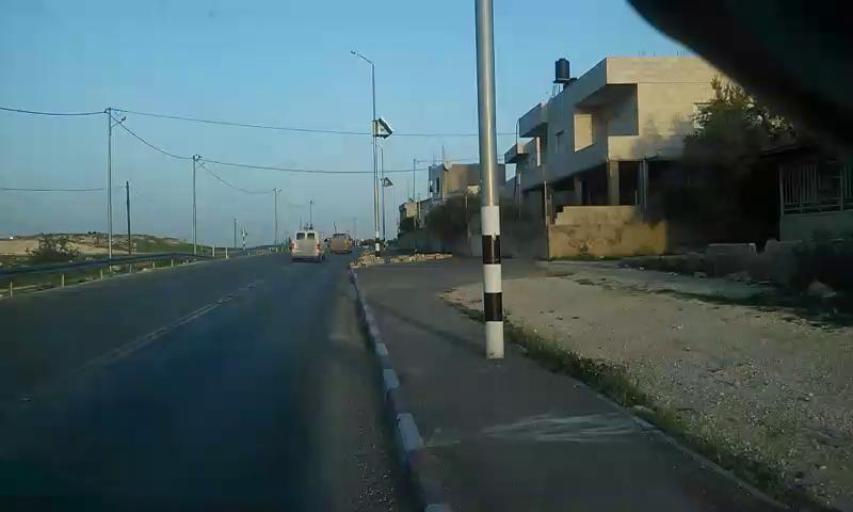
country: PS
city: Al `Ubaydiyah
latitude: 31.7429
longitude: 35.2899
